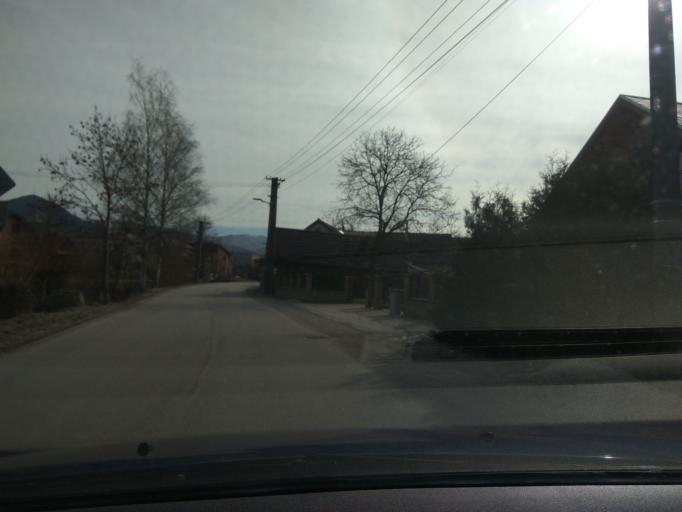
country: SK
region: Zilinsky
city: Rajec
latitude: 49.1179
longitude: 18.6746
